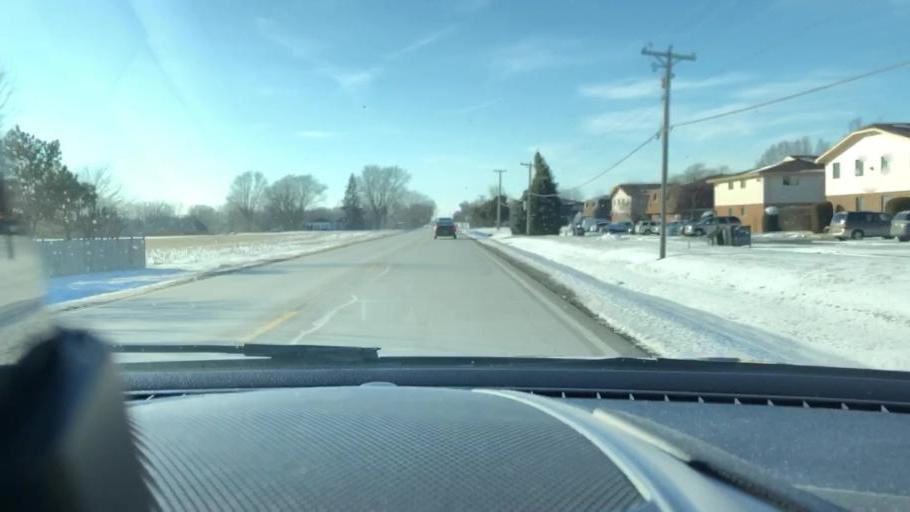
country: US
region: Illinois
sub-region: Will County
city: New Lenox
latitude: 41.4828
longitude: -87.9884
